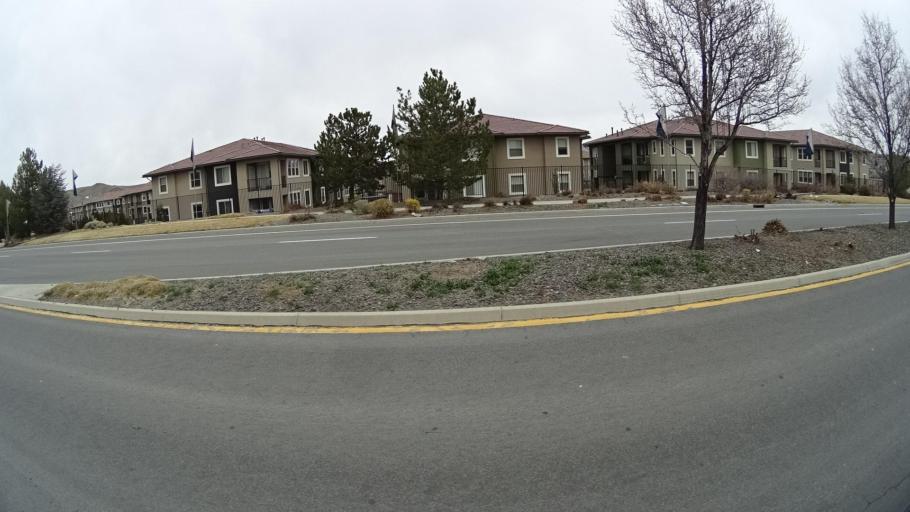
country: US
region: Nevada
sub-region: Washoe County
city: Sun Valley
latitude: 39.5755
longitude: -119.7384
